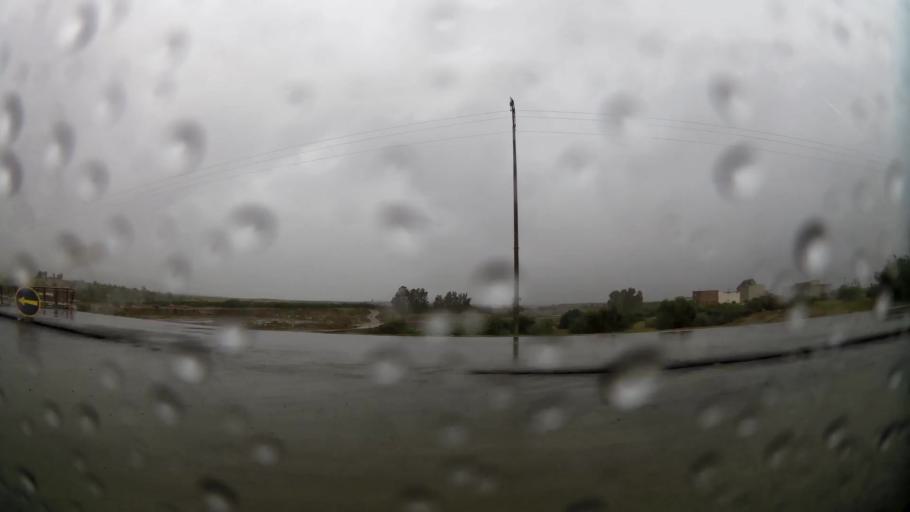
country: MA
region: Oriental
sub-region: Nador
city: Midar
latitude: 34.8779
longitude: -3.7261
